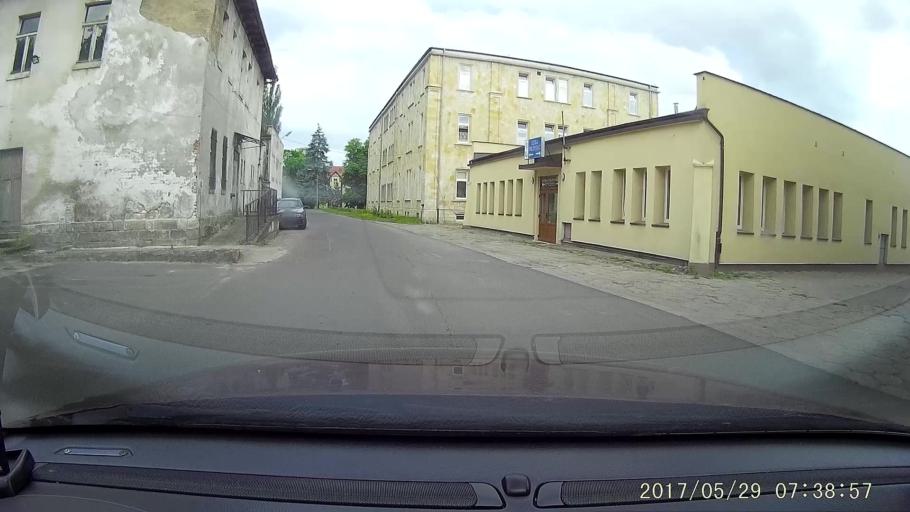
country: PL
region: Lower Silesian Voivodeship
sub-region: Powiat boleslawiecki
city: Boleslawiec
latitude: 51.2598
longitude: 15.5863
